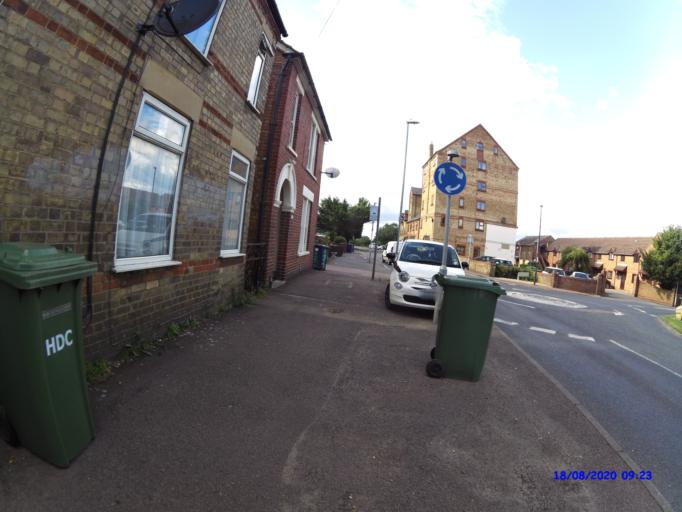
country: GB
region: England
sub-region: Cambridgeshire
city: Ramsey
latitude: 52.4530
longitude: -0.1107
